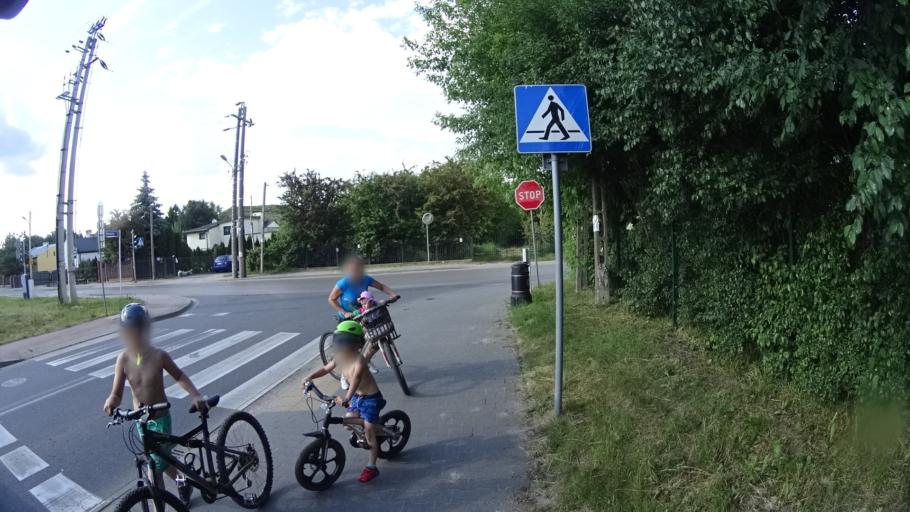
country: PL
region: Masovian Voivodeship
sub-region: Powiat pruszkowski
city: Pruszkow
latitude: 52.1732
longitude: 20.7775
